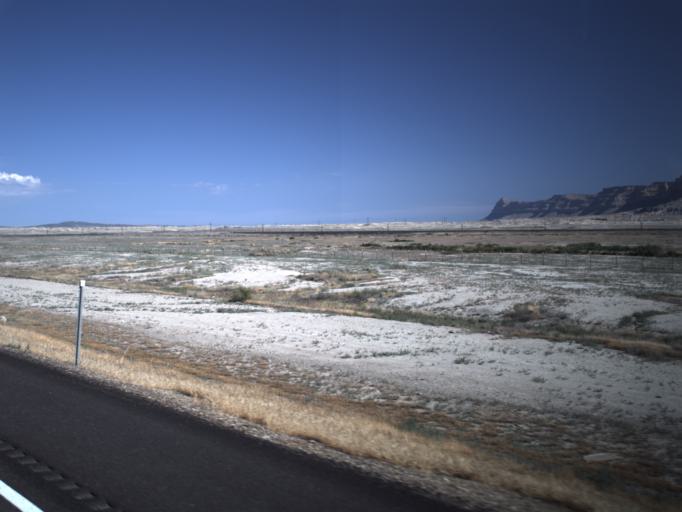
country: US
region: Utah
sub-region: Carbon County
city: East Carbon City
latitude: 38.9965
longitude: -110.2601
